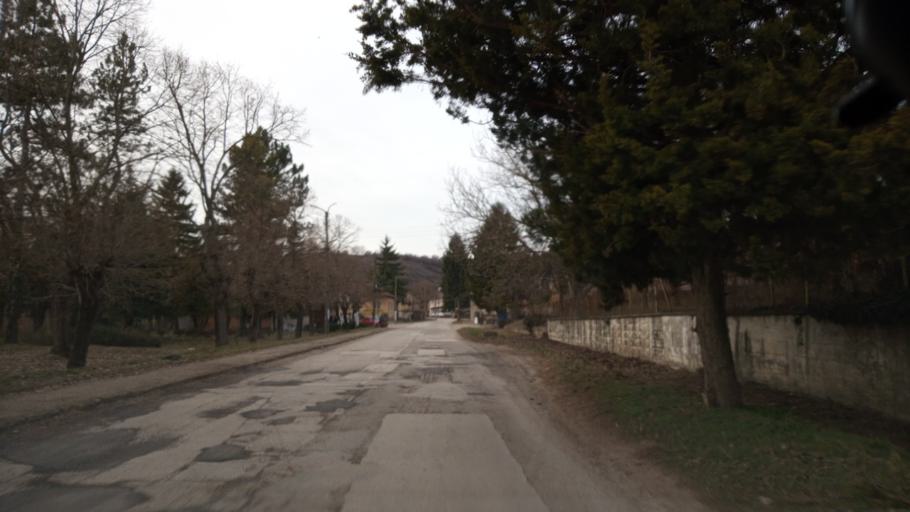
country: BG
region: Pleven
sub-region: Obshtina Belene
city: Belene
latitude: 43.6046
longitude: 25.0004
